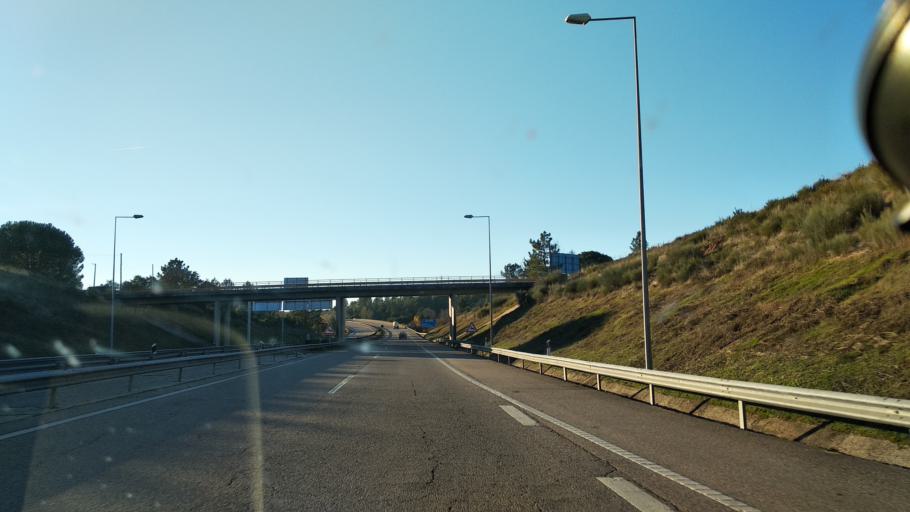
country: PT
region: Santarem
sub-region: Entroncamento
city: Entroncamento
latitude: 39.4893
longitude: -8.4513
